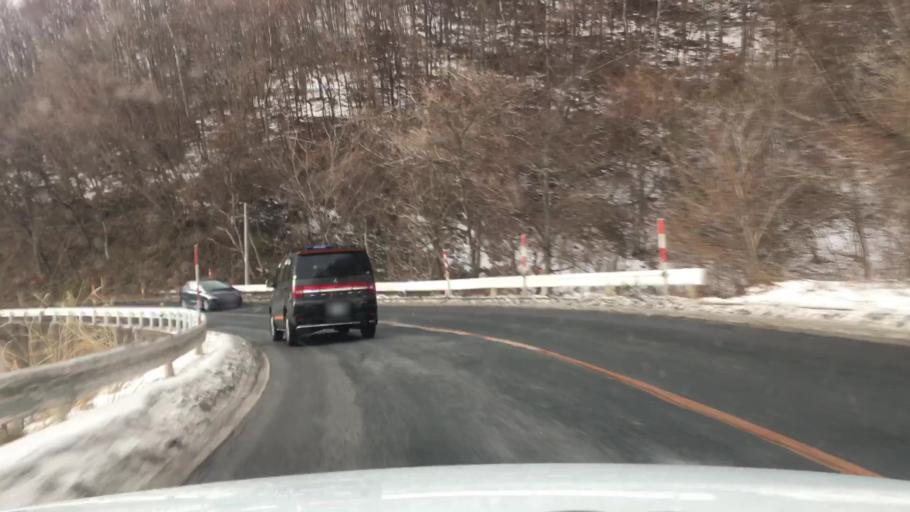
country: JP
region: Iwate
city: Morioka-shi
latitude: 39.6612
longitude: 141.3347
